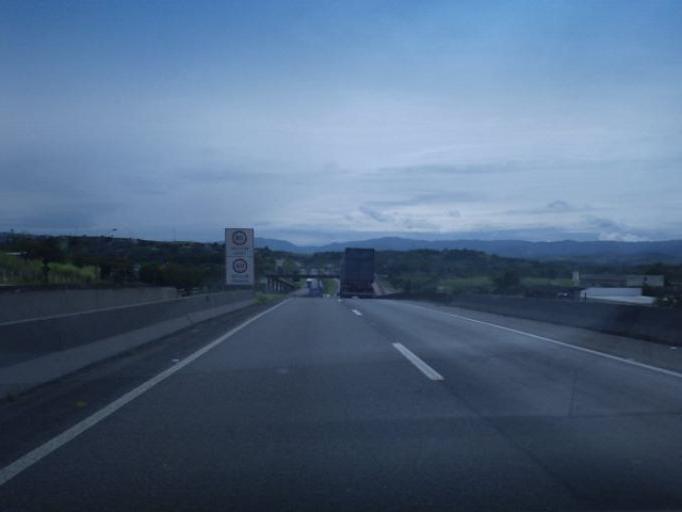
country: BR
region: Sao Paulo
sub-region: Cajati
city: Cajati
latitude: -24.7317
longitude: -48.1107
